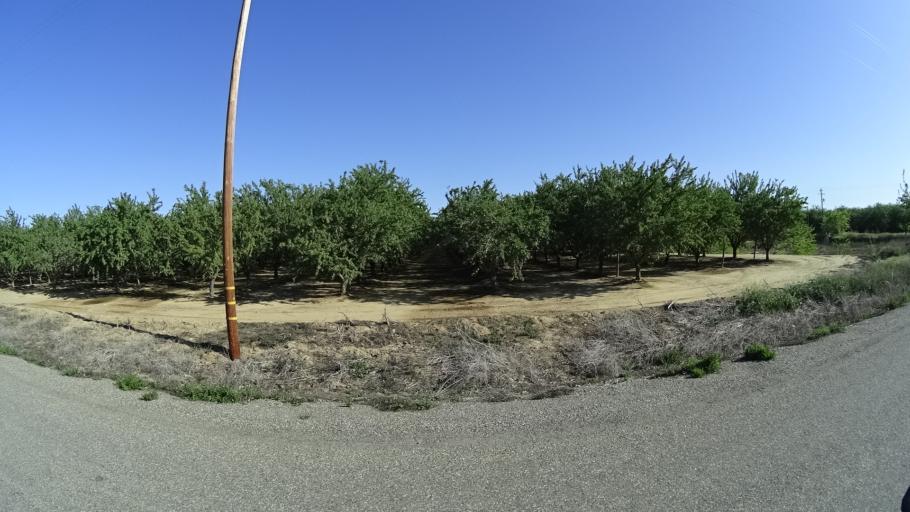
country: US
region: California
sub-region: Glenn County
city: Hamilton City
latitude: 39.6948
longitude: -122.0651
